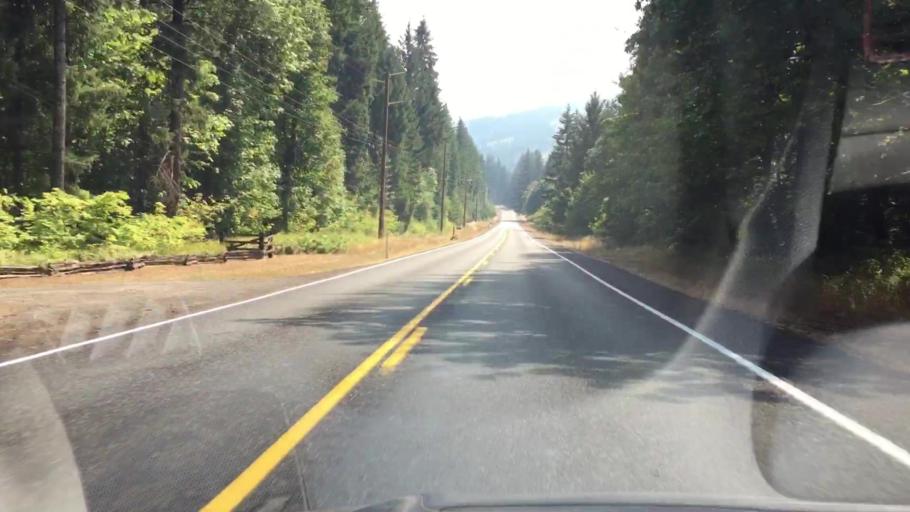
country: US
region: Washington
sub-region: Klickitat County
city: White Salmon
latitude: 45.8594
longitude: -121.5107
